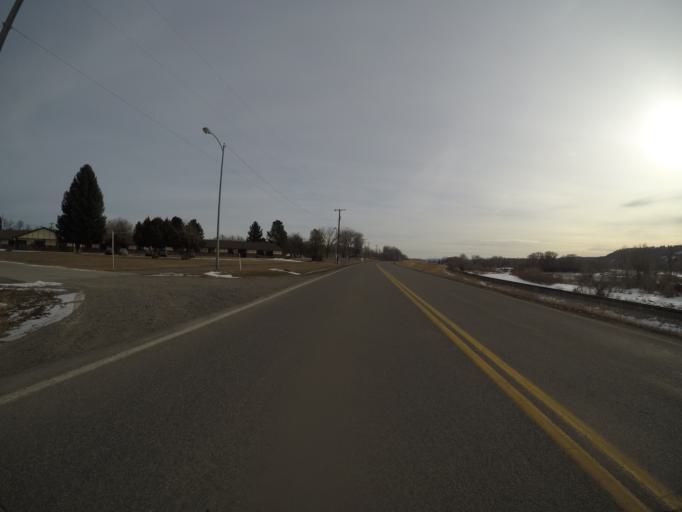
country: US
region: Montana
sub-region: Stillwater County
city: Columbus
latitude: 45.6403
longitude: -109.2657
